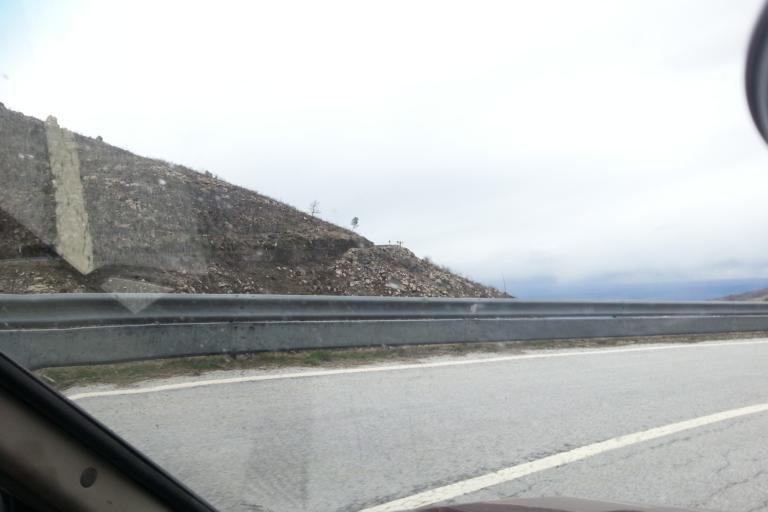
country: PT
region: Guarda
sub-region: Manteigas
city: Manteigas
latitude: 40.4508
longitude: -7.5862
